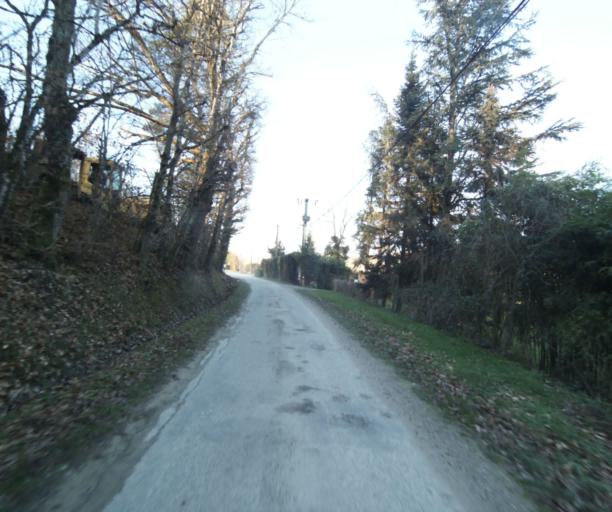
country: FR
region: Midi-Pyrenees
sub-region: Departement du Tarn-et-Garonne
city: Moissac
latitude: 44.1302
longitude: 1.0893
